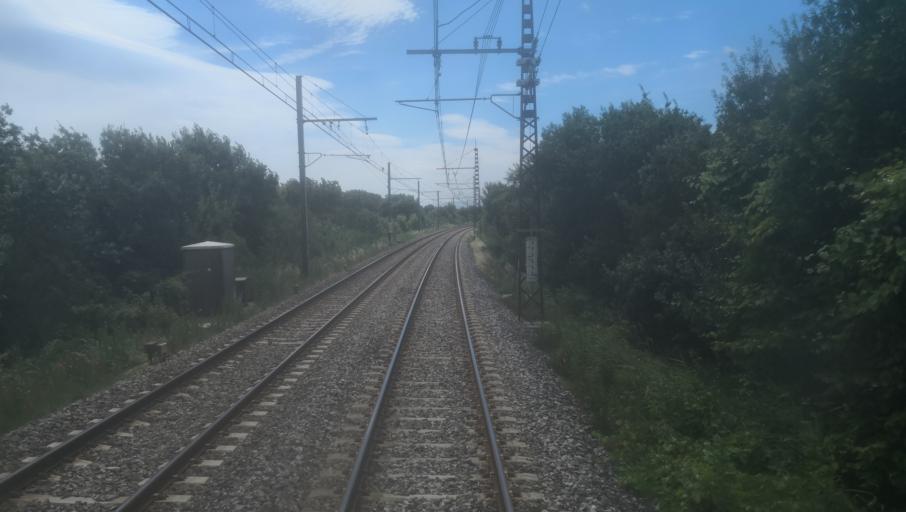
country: FR
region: Languedoc-Roussillon
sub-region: Departement de l'Aude
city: Coursan
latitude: 43.2486
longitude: 3.0666
